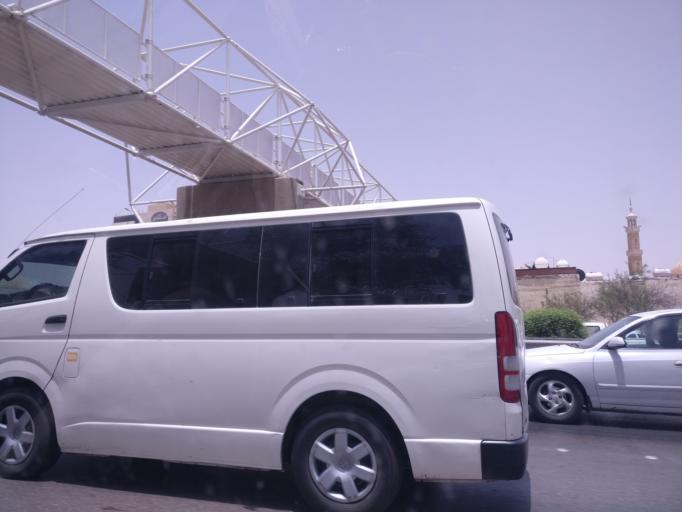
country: SA
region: Ar Riyad
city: Riyadh
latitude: 24.6144
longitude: 46.7069
